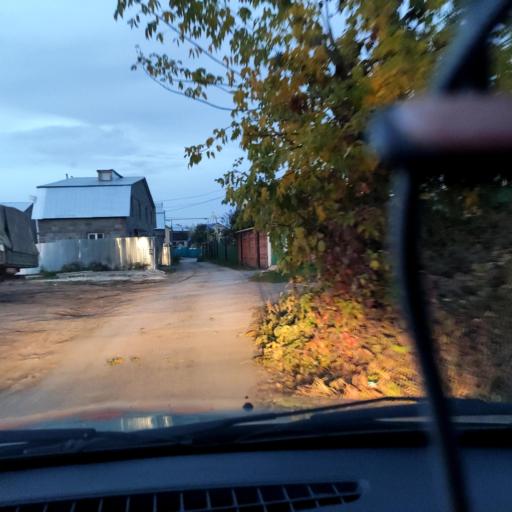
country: RU
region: Bashkortostan
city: Ufa
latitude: 54.7305
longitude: 55.9063
